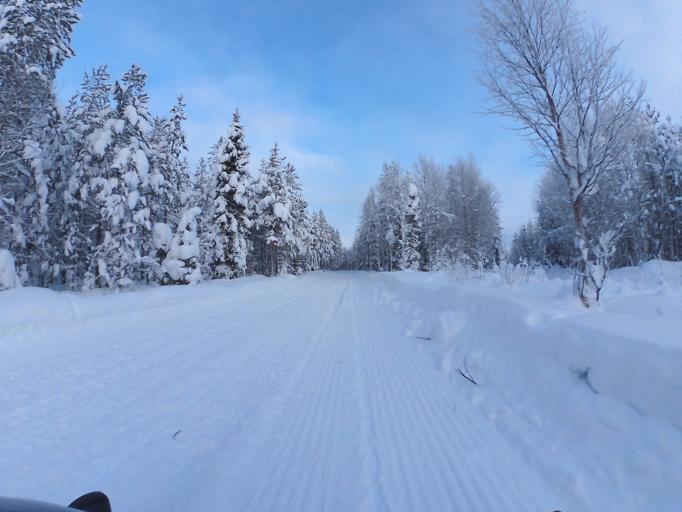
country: FI
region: Lapland
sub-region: Rovaniemi
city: Rovaniemi
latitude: 66.5278
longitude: 26.0314
